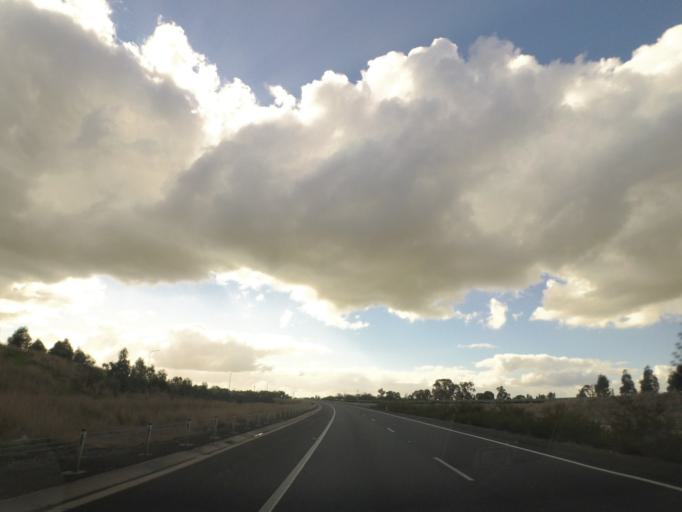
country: AU
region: New South Wales
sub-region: Greater Hume Shire
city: Holbrook
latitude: -35.7326
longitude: 147.3055
